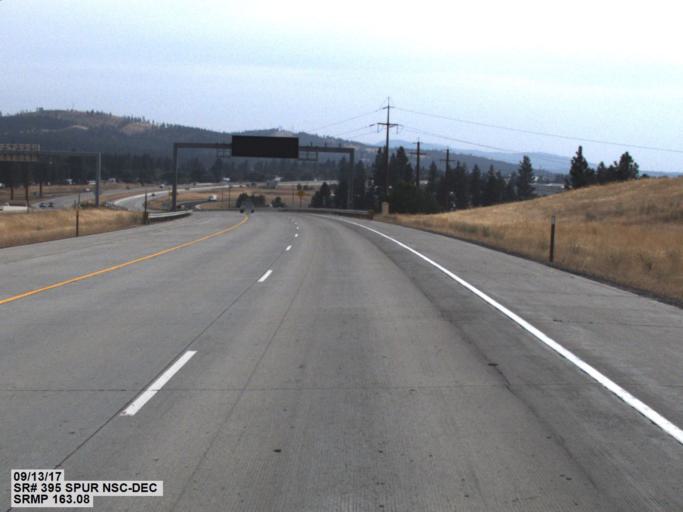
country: US
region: Washington
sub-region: Spokane County
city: Mead
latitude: 47.7367
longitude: -117.3604
